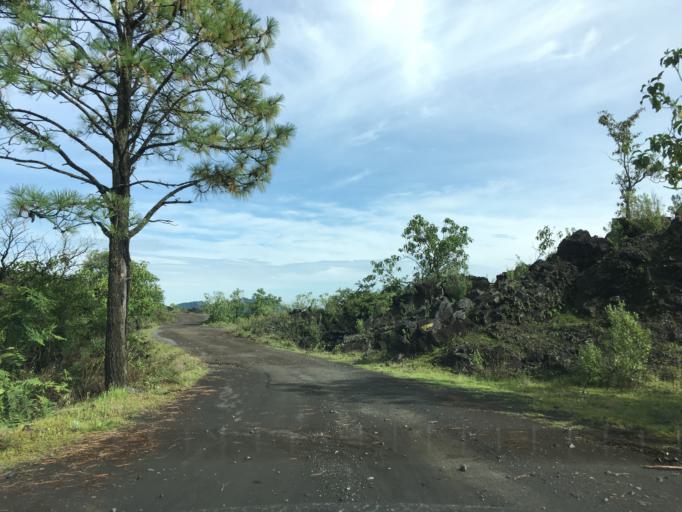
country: MX
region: Michoacan
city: Angahuan
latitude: 19.5213
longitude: -102.2260
